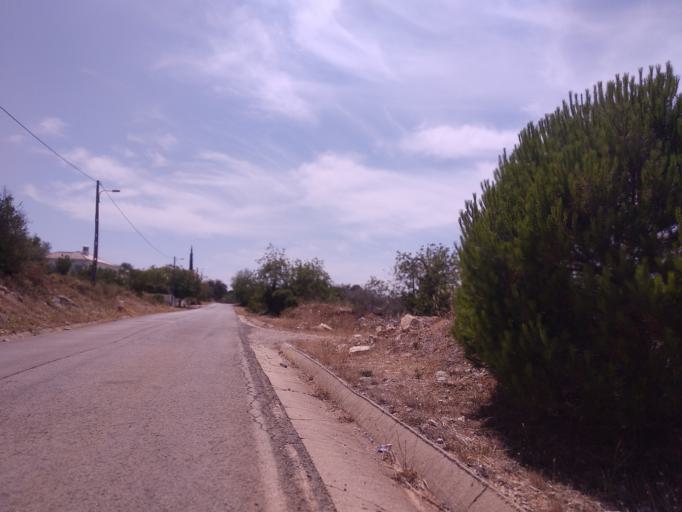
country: PT
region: Faro
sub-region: Faro
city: Santa Barbara de Nexe
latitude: 37.1260
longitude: -7.9366
